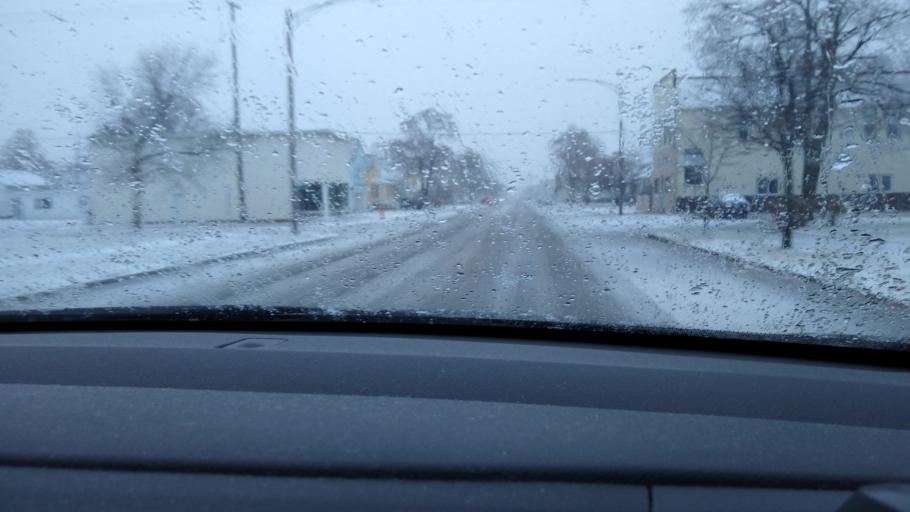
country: US
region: Michigan
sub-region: Delta County
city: Escanaba
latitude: 45.7406
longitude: -87.0612
